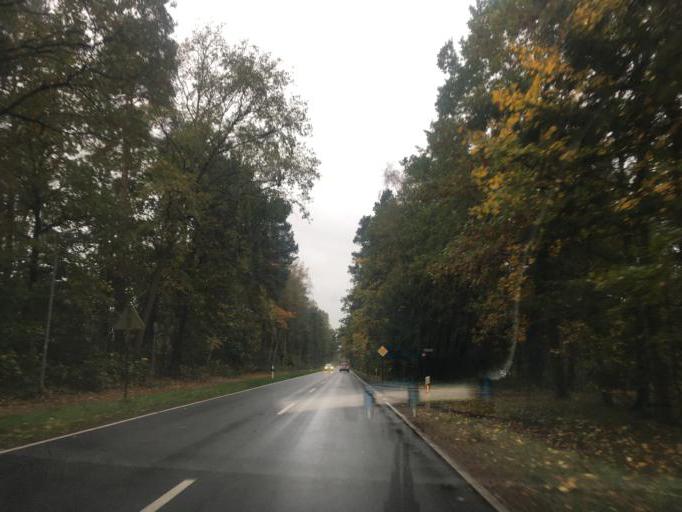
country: DE
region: Lower Saxony
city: Winsen
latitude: 52.6416
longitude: 9.9328
